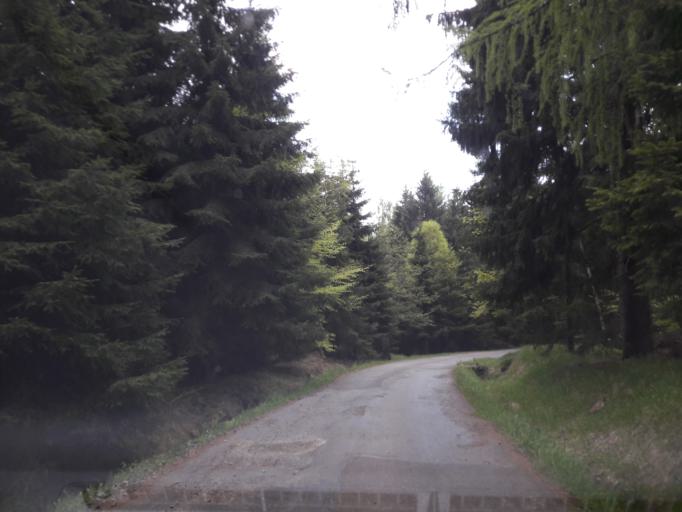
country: CZ
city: Machov
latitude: 50.4665
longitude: 16.2956
